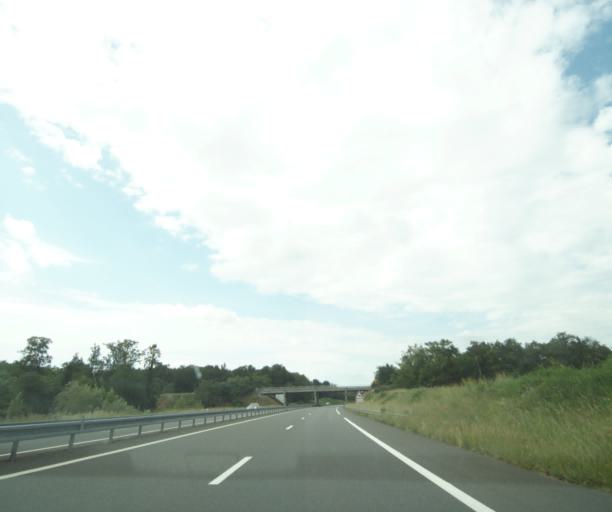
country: FR
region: Pays de la Loire
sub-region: Departement de Maine-et-Loire
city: Brion
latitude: 47.4416
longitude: -0.1751
